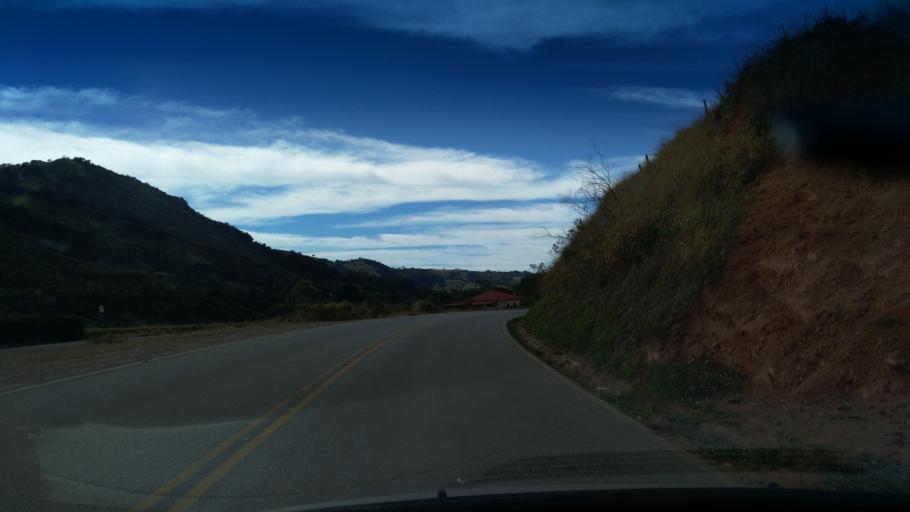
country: BR
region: Minas Gerais
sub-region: Andradas
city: Andradas
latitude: -22.0568
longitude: -46.4298
